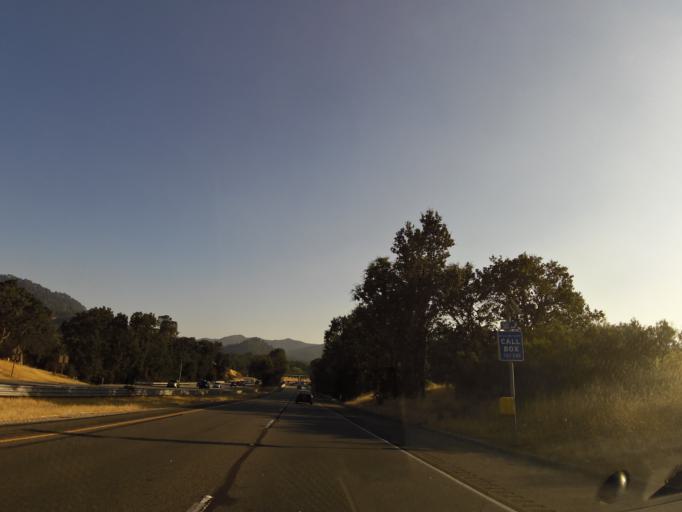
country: US
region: California
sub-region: San Luis Obispo County
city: Santa Margarita
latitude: 35.3871
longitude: -120.6279
